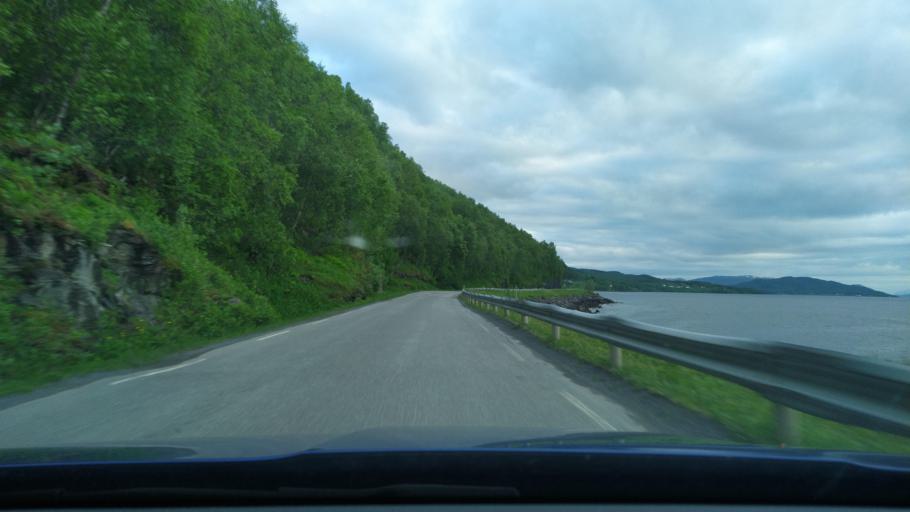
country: NO
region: Troms
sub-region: Lenvik
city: Finnsnes
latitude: 69.1442
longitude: 17.9229
